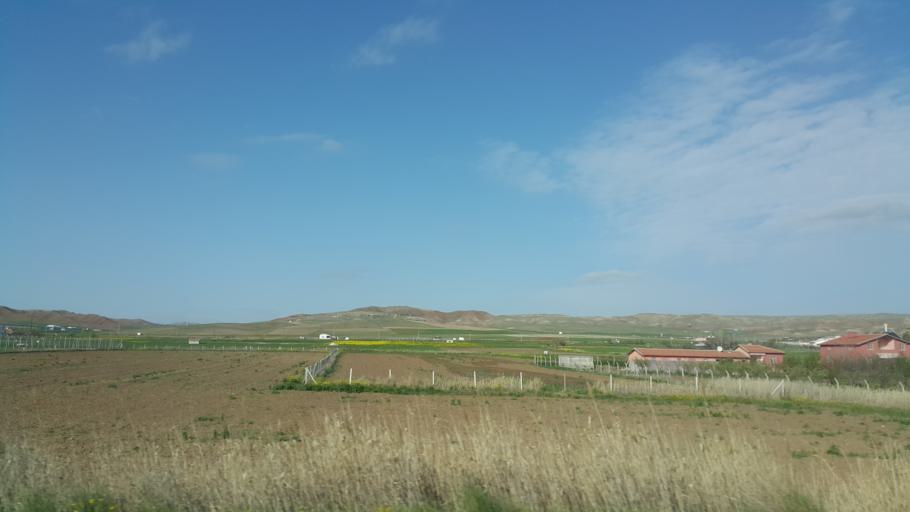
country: TR
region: Aksaray
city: Acipinar
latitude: 38.5014
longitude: 33.8672
